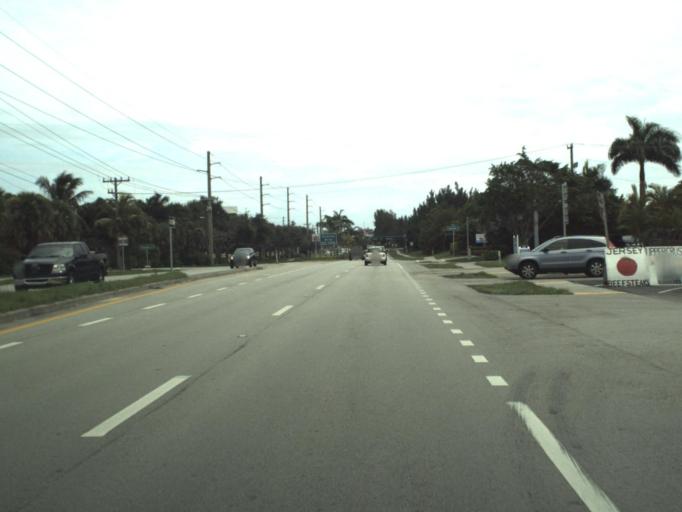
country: US
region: Florida
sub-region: Palm Beach County
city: Juno Beach
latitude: 26.8547
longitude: -80.0576
